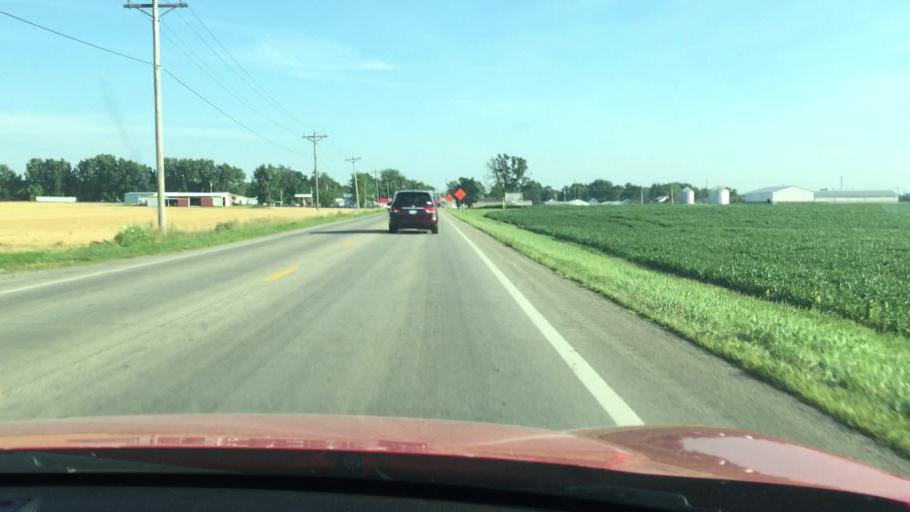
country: US
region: Ohio
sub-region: Logan County
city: Northwood
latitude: 40.4515
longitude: -83.8074
